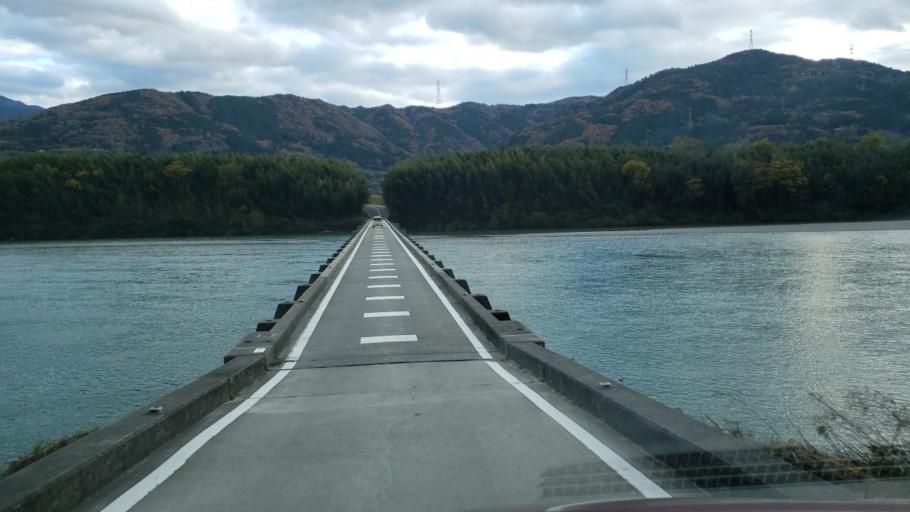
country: JP
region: Tokushima
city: Wakimachi
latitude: 34.0659
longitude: 134.1431
